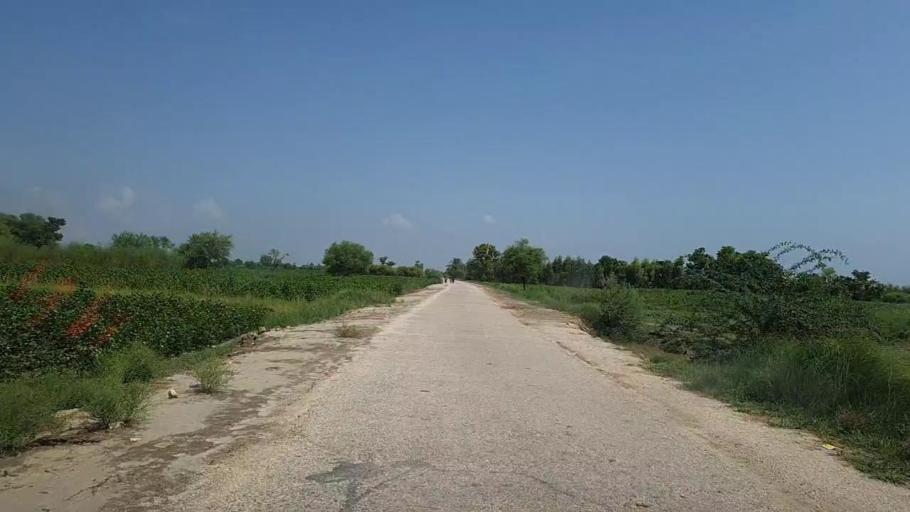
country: PK
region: Sindh
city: Bhiria
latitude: 26.8955
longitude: 68.2211
